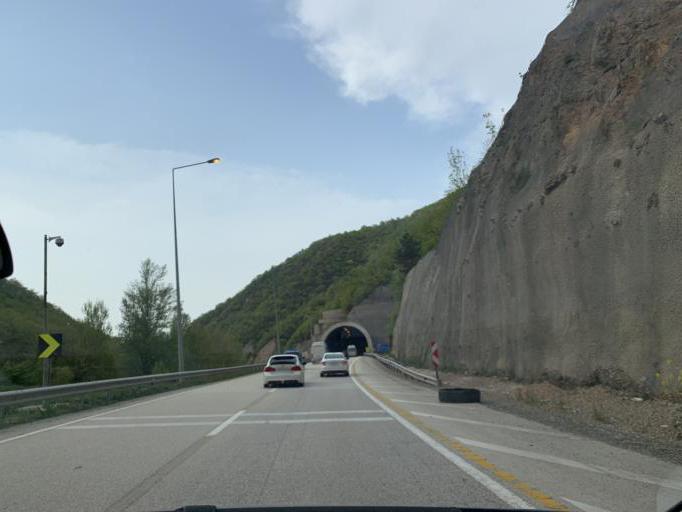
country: TR
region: Bursa
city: Kursunlu
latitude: 40.0042
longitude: 29.6521
